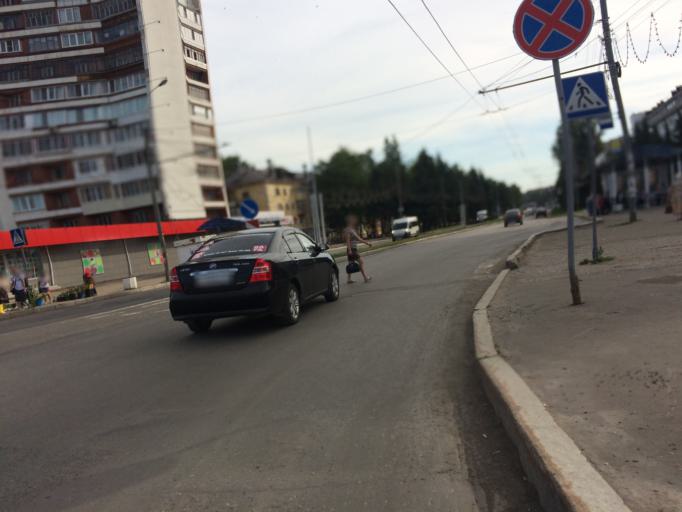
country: RU
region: Mariy-El
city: Yoshkar-Ola
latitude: 56.6222
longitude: 47.8814
